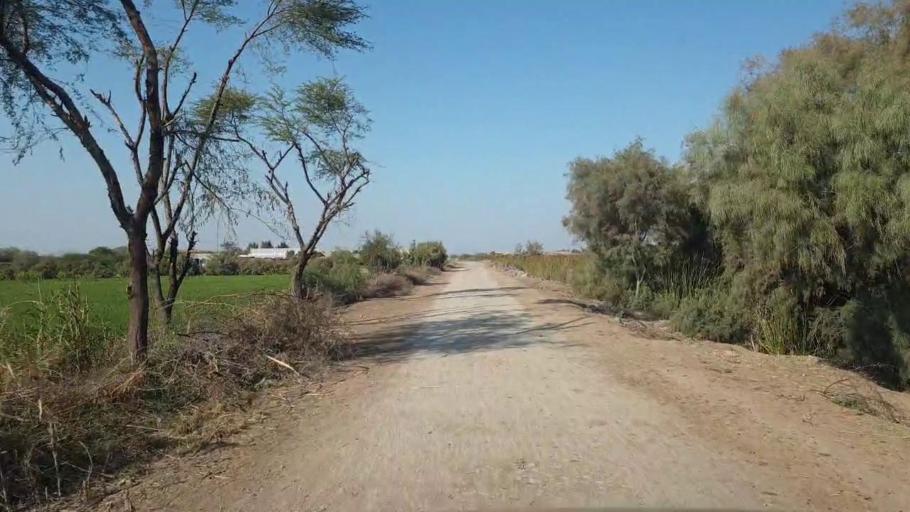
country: PK
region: Sindh
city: Shahpur Chakar
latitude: 26.1706
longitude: 68.6811
